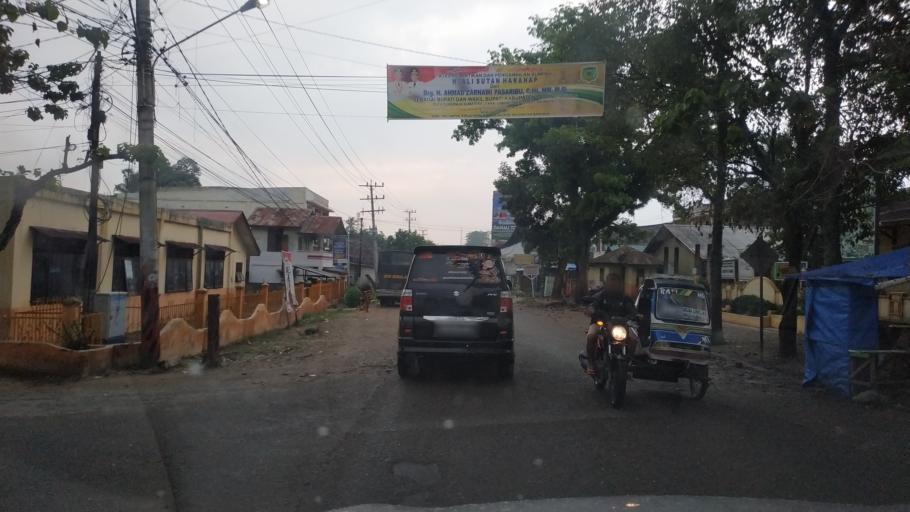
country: ID
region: North Sumatra
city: Sibubuhan
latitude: 1.0525
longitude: 99.7319
